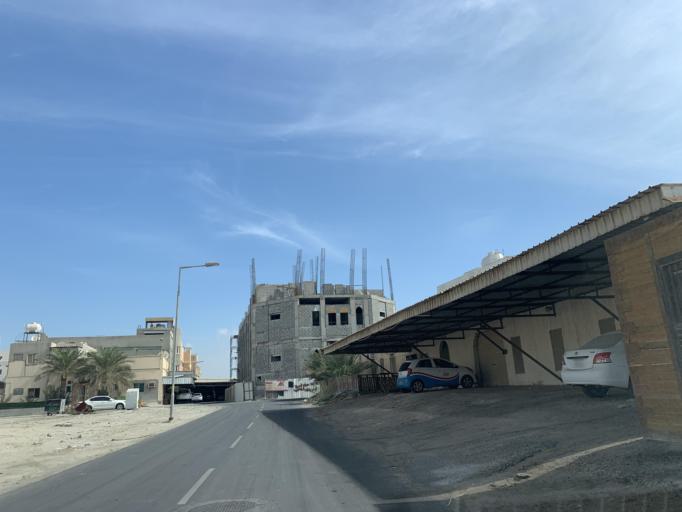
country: BH
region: Central Governorate
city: Madinat Hamad
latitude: 26.1255
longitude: 50.4749
